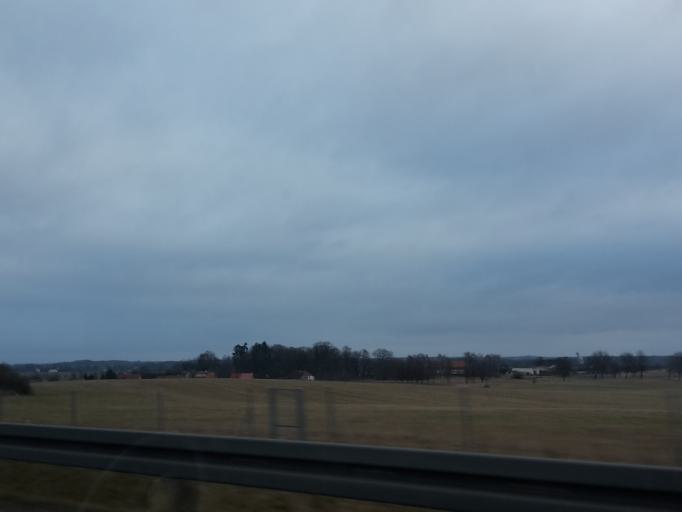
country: PL
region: Warmian-Masurian Voivodeship
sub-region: Powiat ostrodzki
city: Maldyty
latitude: 53.8664
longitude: 19.7452
